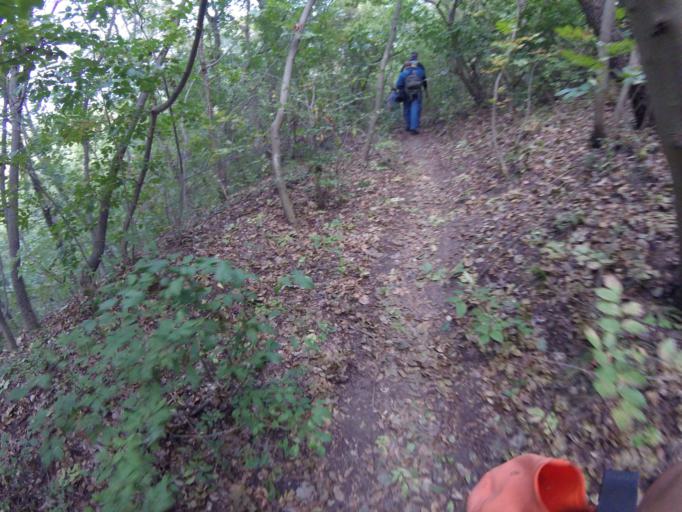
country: HU
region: Pest
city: Fot
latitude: 47.6271
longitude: 19.2077
